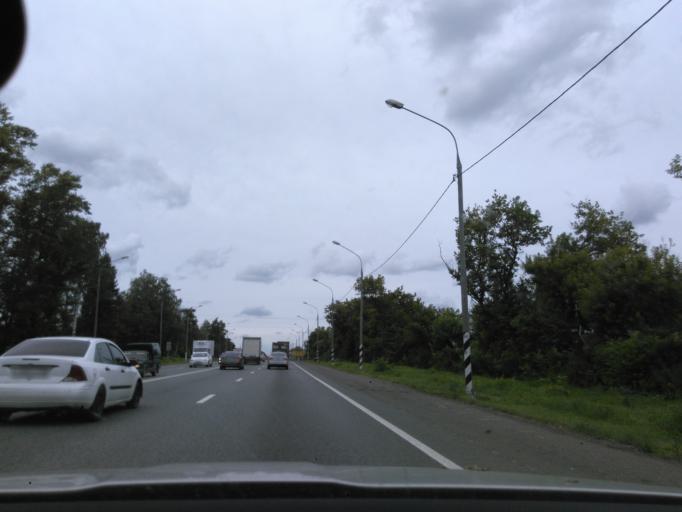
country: RU
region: Moskovskaya
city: Klin
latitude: 56.3037
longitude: 36.7897
